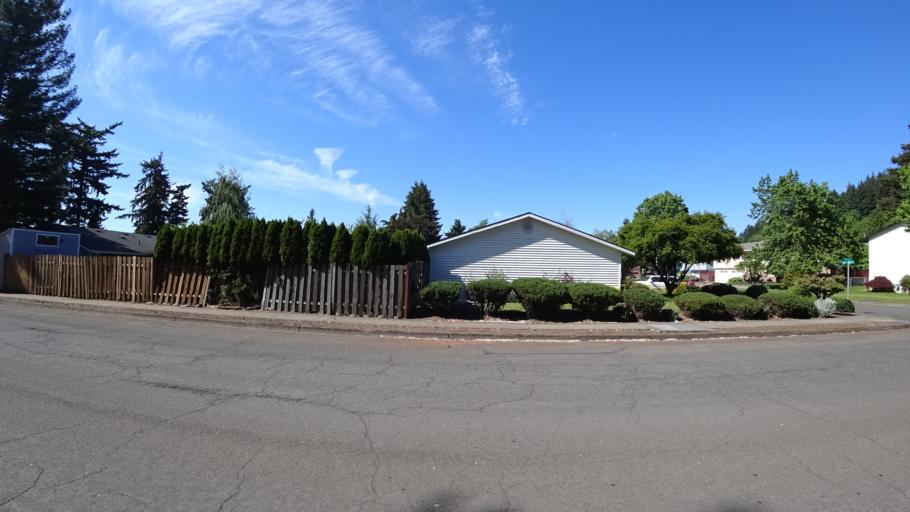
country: US
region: Oregon
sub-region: Multnomah County
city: Gresham
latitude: 45.4980
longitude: -122.4743
